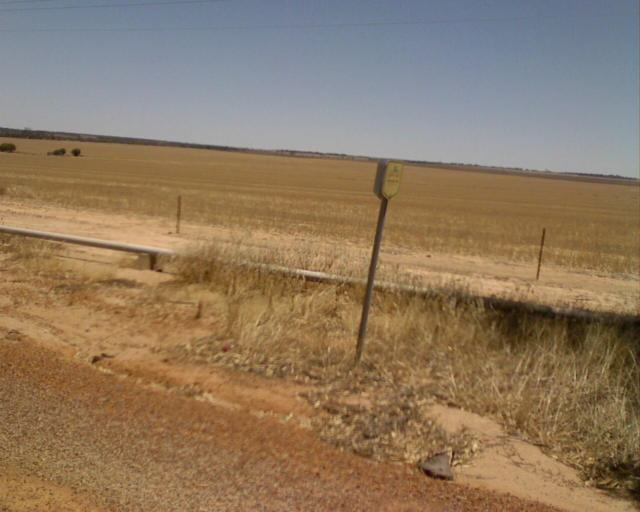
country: AU
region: Western Australia
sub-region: Merredin
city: Merredin
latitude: -30.8186
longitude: 117.8624
